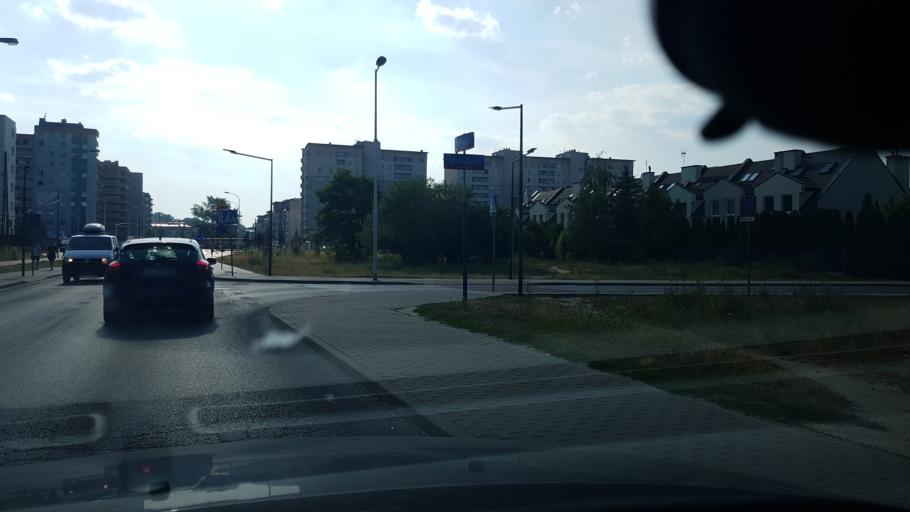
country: PL
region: Masovian Voivodeship
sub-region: Warszawa
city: Bialoleka
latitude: 52.3323
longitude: 20.9445
